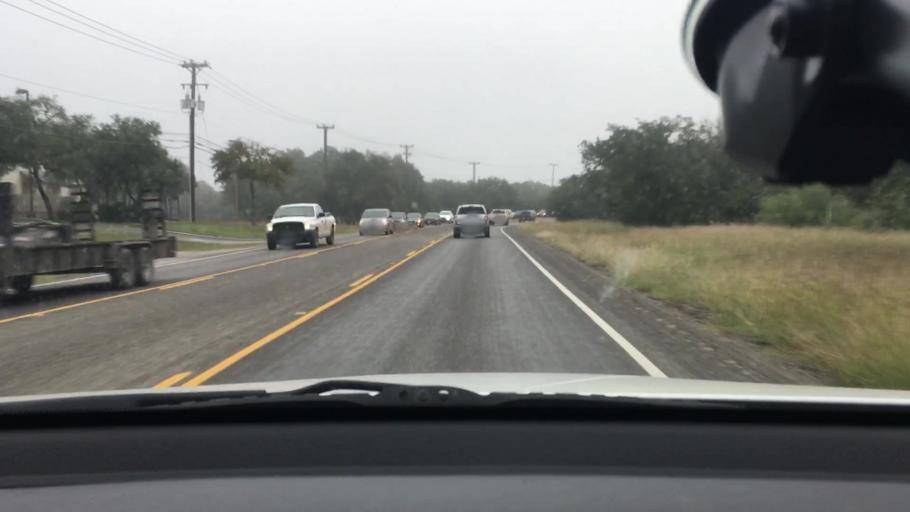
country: US
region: Texas
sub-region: Comal County
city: Garden Ridge
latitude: 29.6211
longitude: -98.3035
